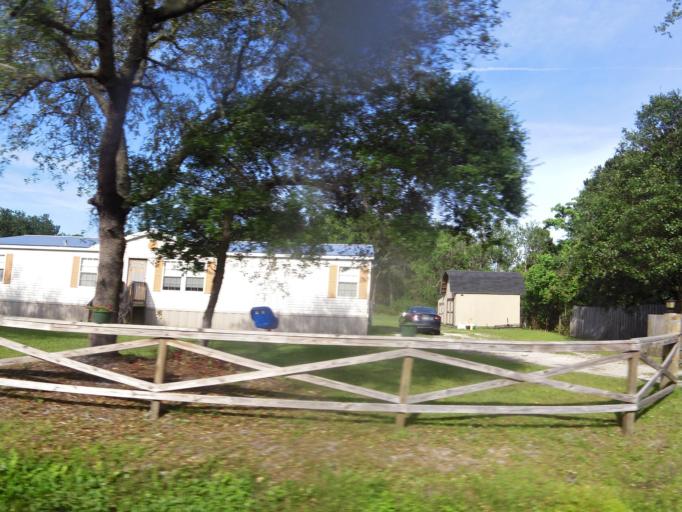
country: US
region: Florida
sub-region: Nassau County
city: Fernandina Beach
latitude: 30.5285
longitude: -81.4839
